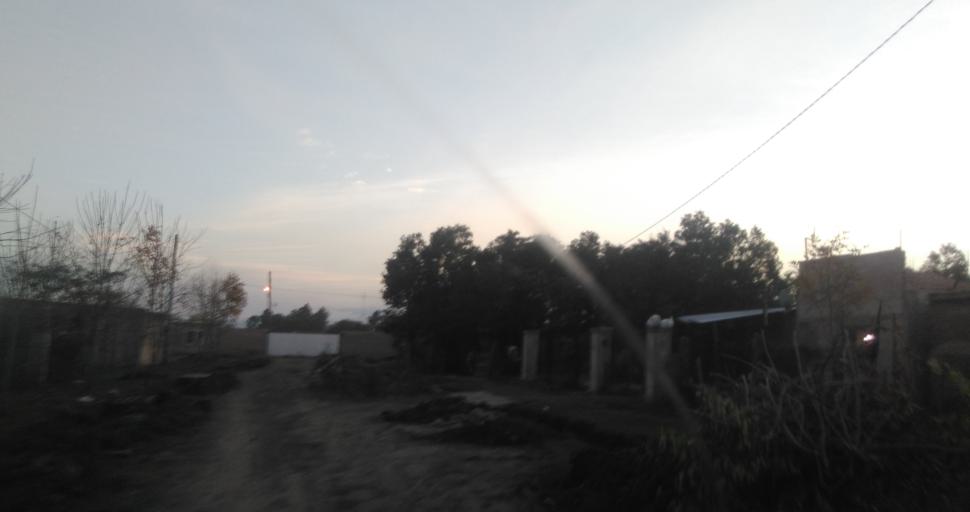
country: AR
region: Chaco
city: Resistencia
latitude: -27.4687
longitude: -59.0174
